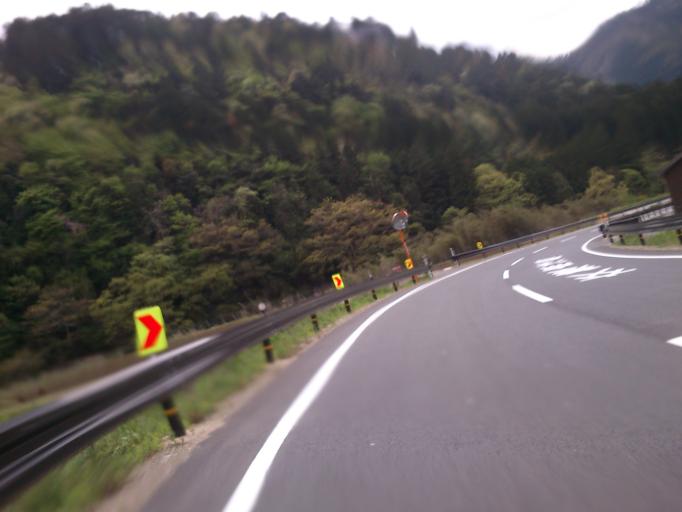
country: JP
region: Fukui
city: Obama
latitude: 35.2962
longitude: 135.6135
